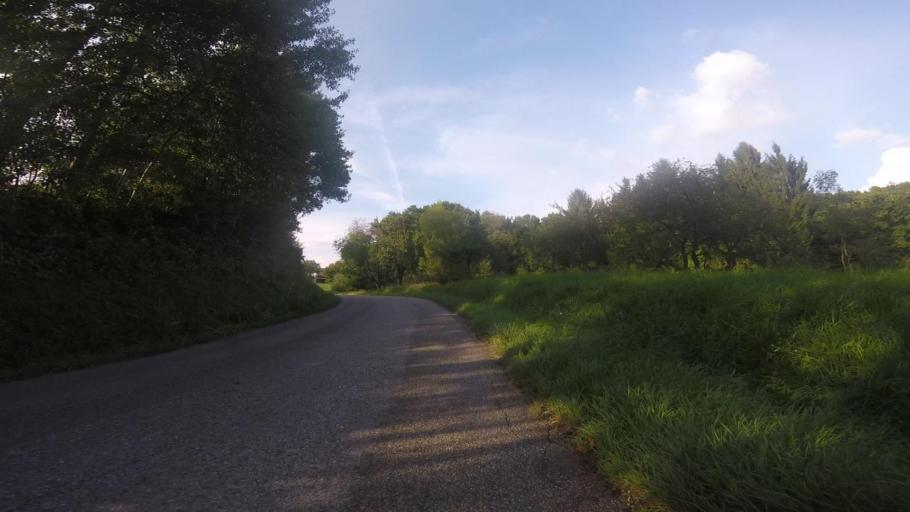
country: DE
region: Baden-Wuerttemberg
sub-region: Regierungsbezirk Stuttgart
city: Aspach
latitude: 49.0007
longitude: 9.3806
